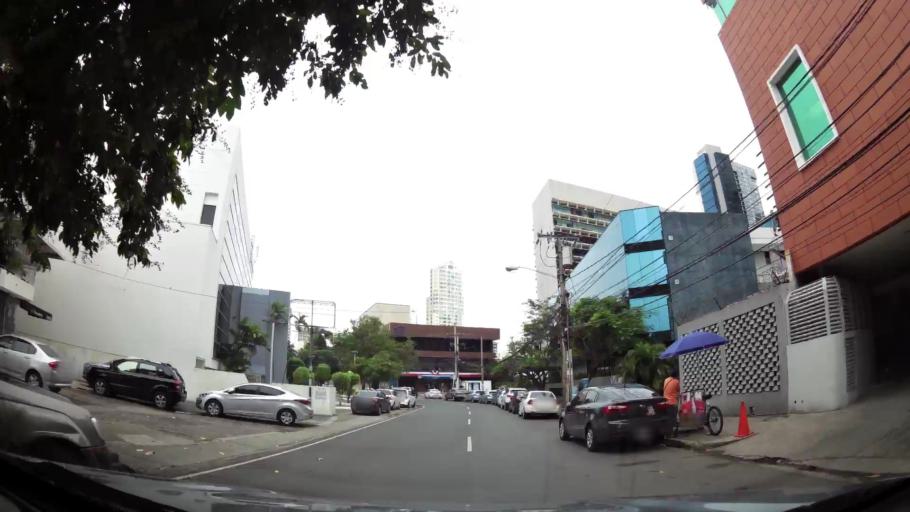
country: PA
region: Panama
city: Panama
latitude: 8.9779
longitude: -79.5238
